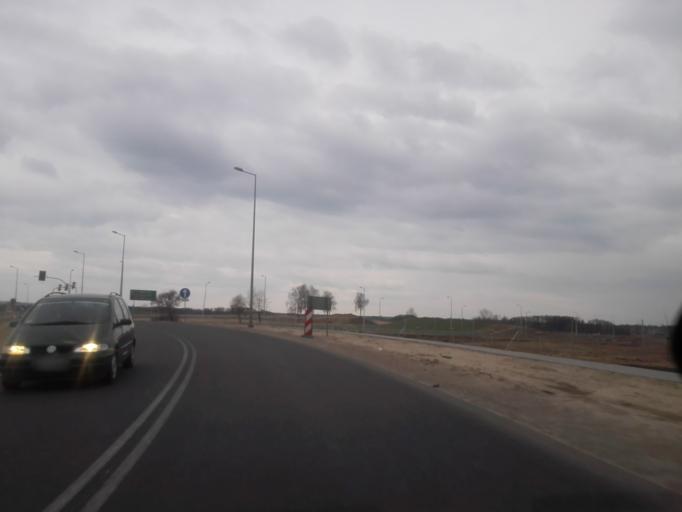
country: PL
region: Podlasie
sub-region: Powiat grajewski
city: Rajgrod
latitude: 53.7499
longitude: 22.7658
